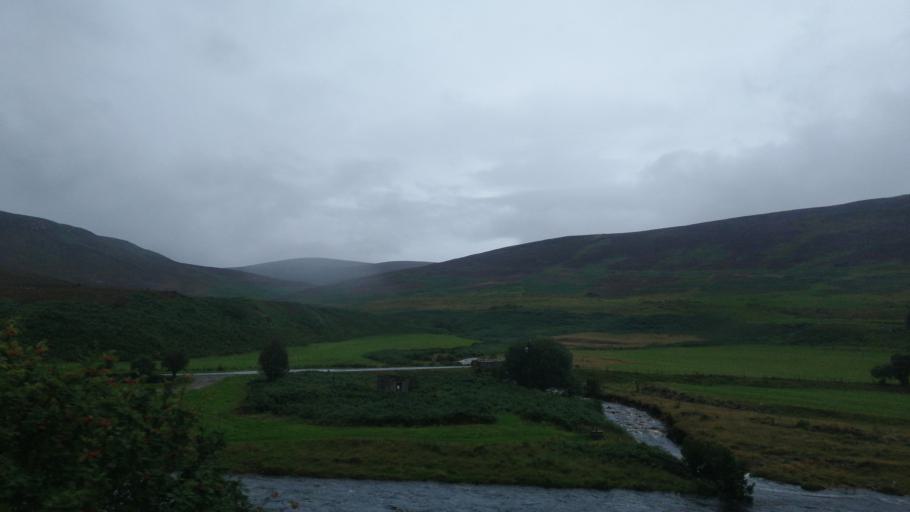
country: GB
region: Scotland
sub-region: Highland
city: Brora
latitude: 58.1354
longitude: -3.6745
